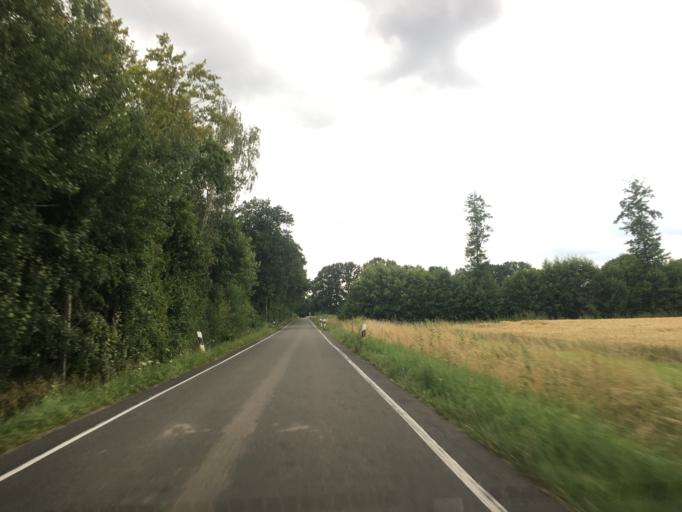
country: DE
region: North Rhine-Westphalia
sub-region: Regierungsbezirk Munster
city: Telgte
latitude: 51.9485
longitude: 7.7156
